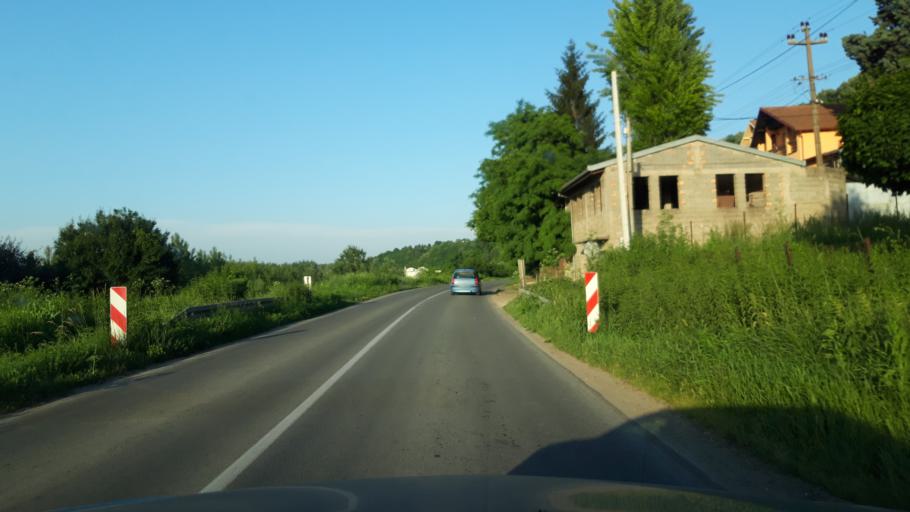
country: RS
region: Autonomna Pokrajina Vojvodina
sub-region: Juznobacki Okrug
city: Beocin
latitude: 45.2090
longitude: 19.7545
